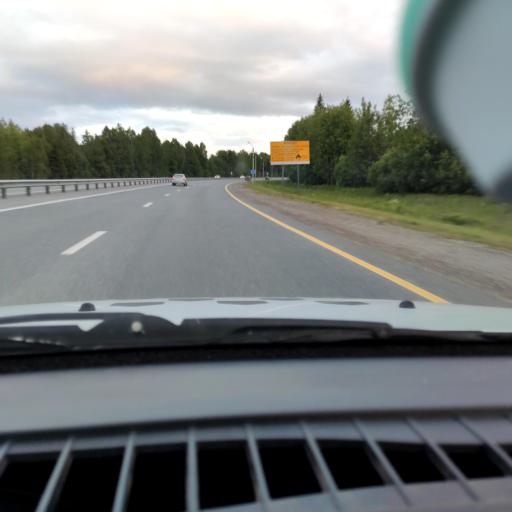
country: RU
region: Perm
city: Polazna
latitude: 58.2363
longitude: 56.4241
